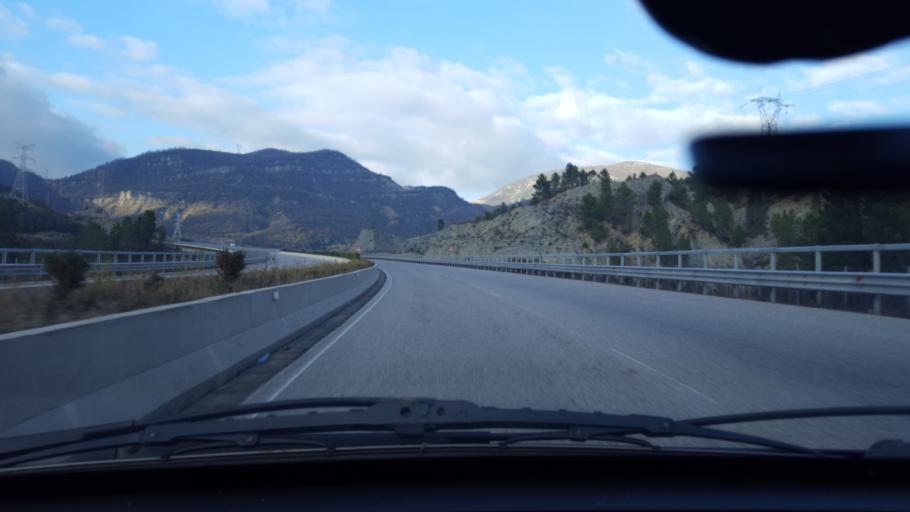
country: AL
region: Tirane
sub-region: Rrethi i Tiranes
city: Krrabe
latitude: 41.1849
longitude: 19.9950
